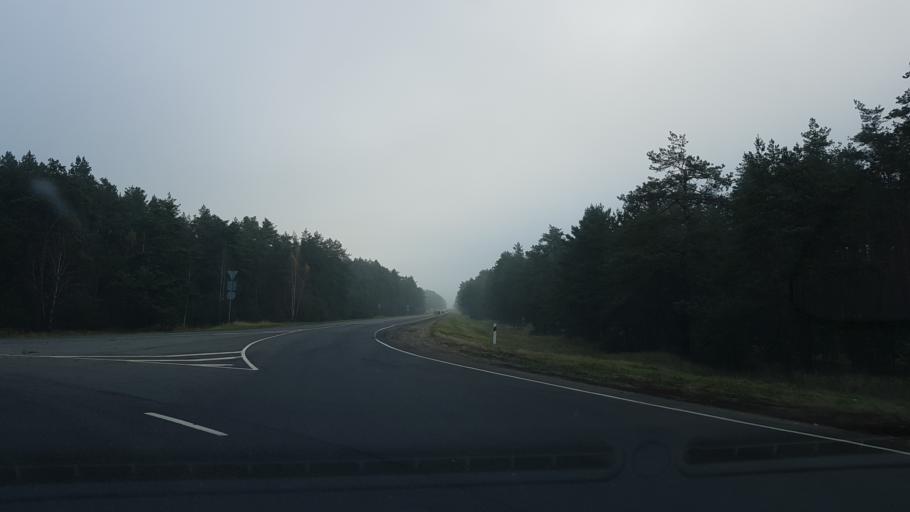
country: BY
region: Mogilev
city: Babruysk
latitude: 53.1560
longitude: 29.3163
